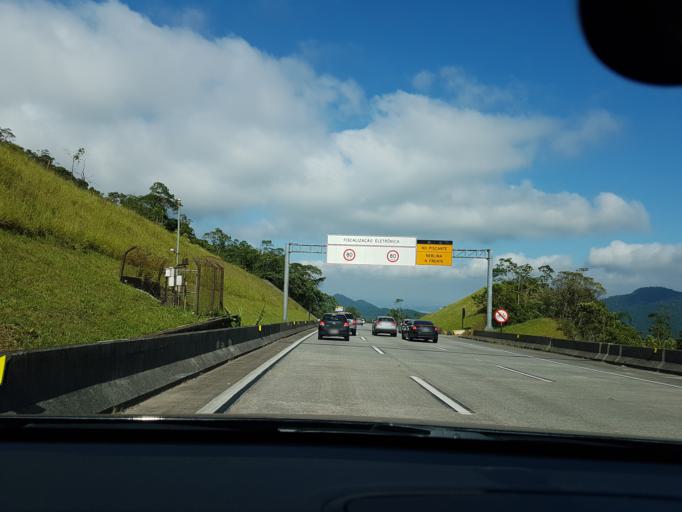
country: BR
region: Sao Paulo
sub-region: Cubatao
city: Cubatao
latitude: -23.9252
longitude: -46.5388
